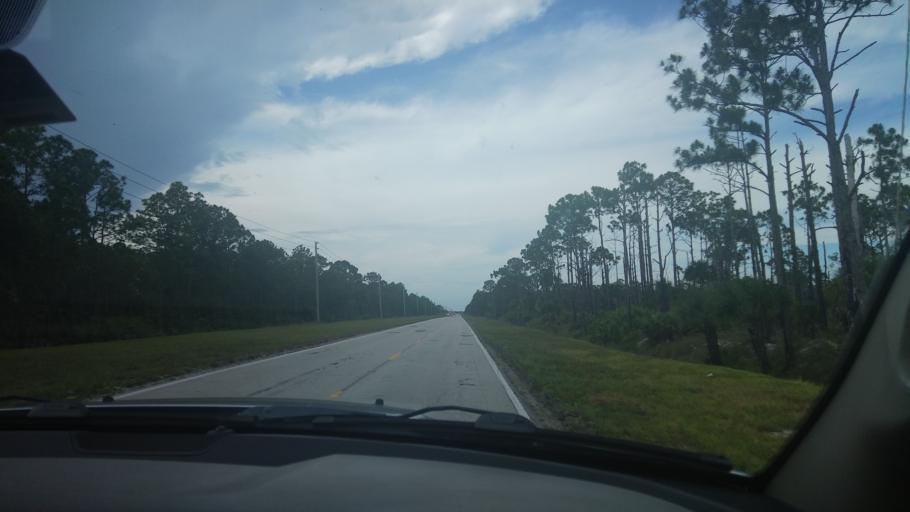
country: US
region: Florida
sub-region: Brevard County
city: Grant-Valkaria
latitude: 27.8793
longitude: -80.6226
